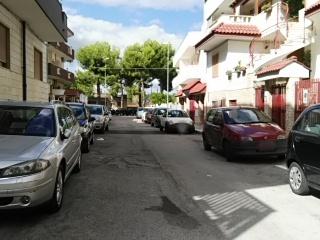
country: IT
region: Apulia
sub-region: Provincia di Bari
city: Triggiano
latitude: 41.0648
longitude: 16.9173
